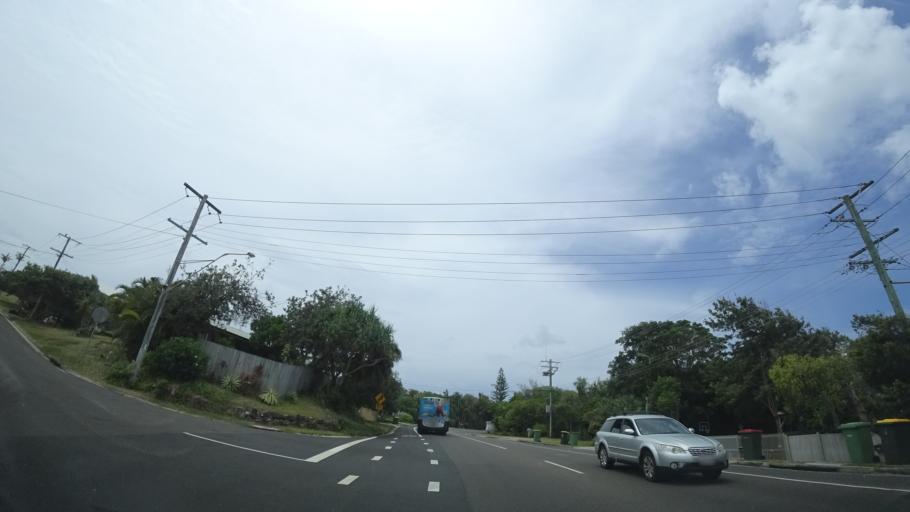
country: AU
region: Queensland
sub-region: Sunshine Coast
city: Coolum Beach
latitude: -26.5507
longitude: 153.0991
